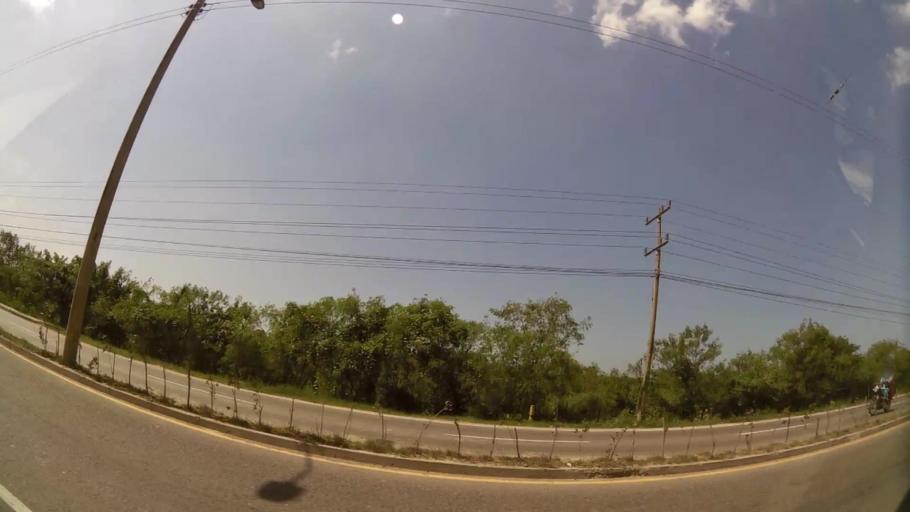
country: CO
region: Bolivar
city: Cartagena
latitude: 10.3488
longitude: -75.4950
